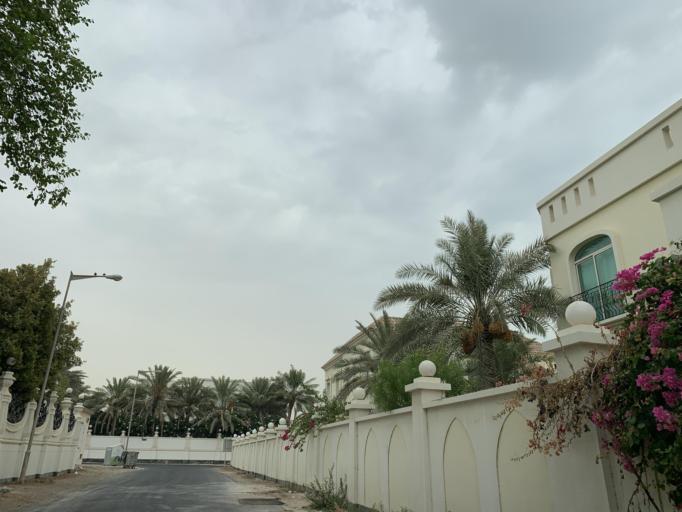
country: BH
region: Northern
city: Madinat `Isa
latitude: 26.1928
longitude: 50.4730
